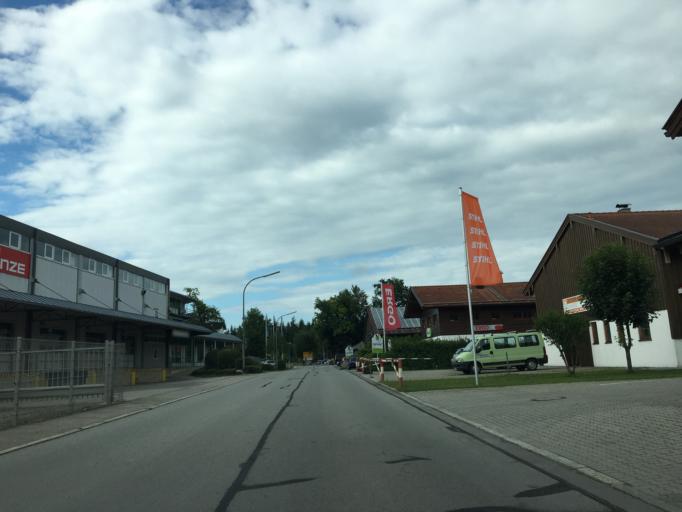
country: DE
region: Bavaria
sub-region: Upper Bavaria
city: Holzkirchen
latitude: 47.8795
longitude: 11.7164
